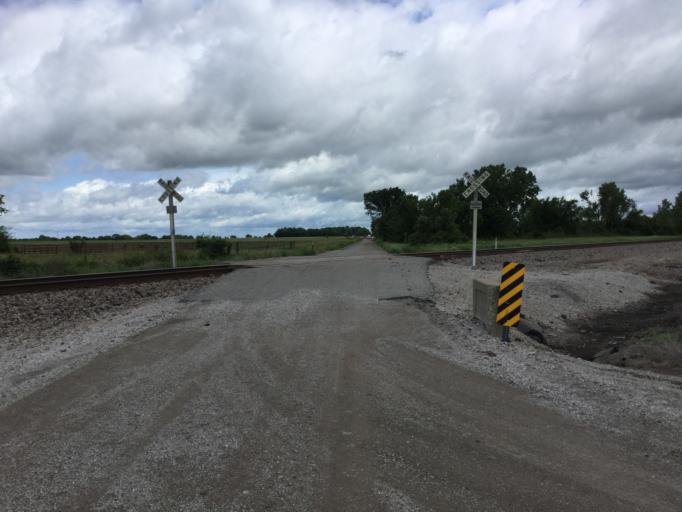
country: US
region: Kansas
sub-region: Bourbon County
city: Fort Scott
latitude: 37.6992
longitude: -94.7955
